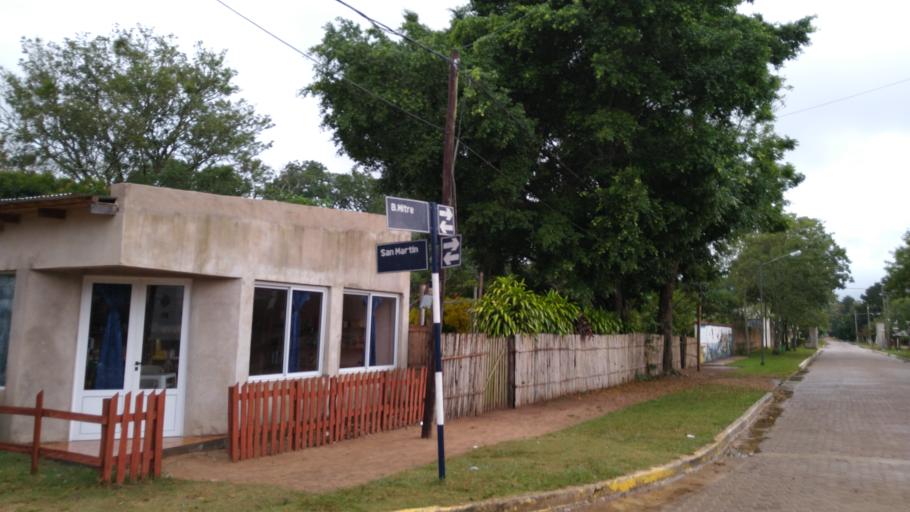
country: AR
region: Corrientes
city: Loreto
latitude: -27.7694
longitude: -57.2814
